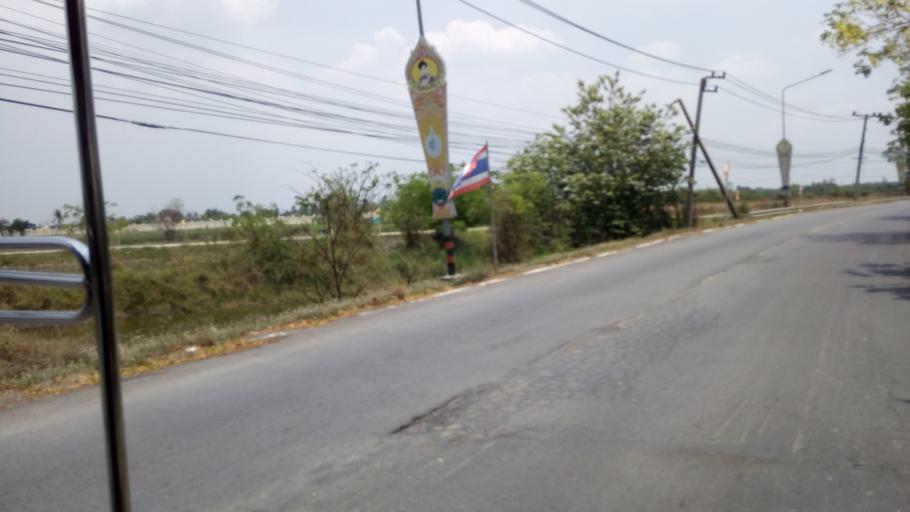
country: TH
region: Pathum Thani
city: Sam Khok
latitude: 14.1118
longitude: 100.5386
